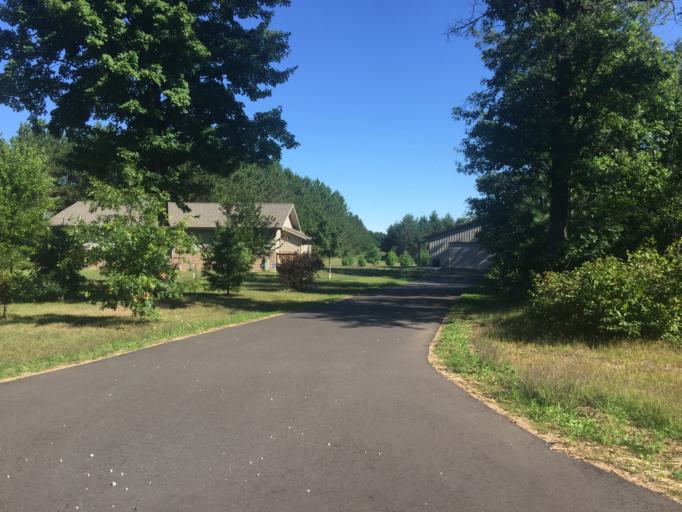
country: US
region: Wisconsin
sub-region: Oconto County
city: Oconto Falls
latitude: 45.3000
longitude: -88.1364
